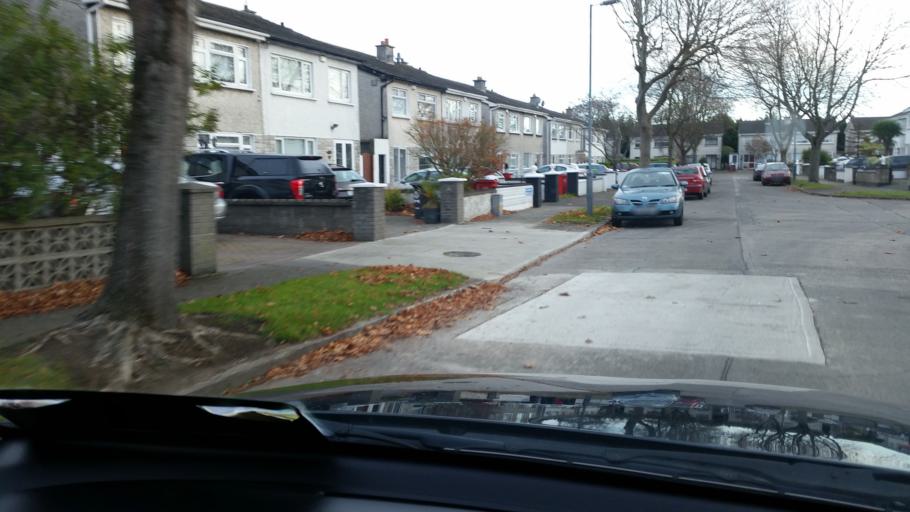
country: IE
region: Leinster
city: Beaumont
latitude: 53.3943
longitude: -6.2448
